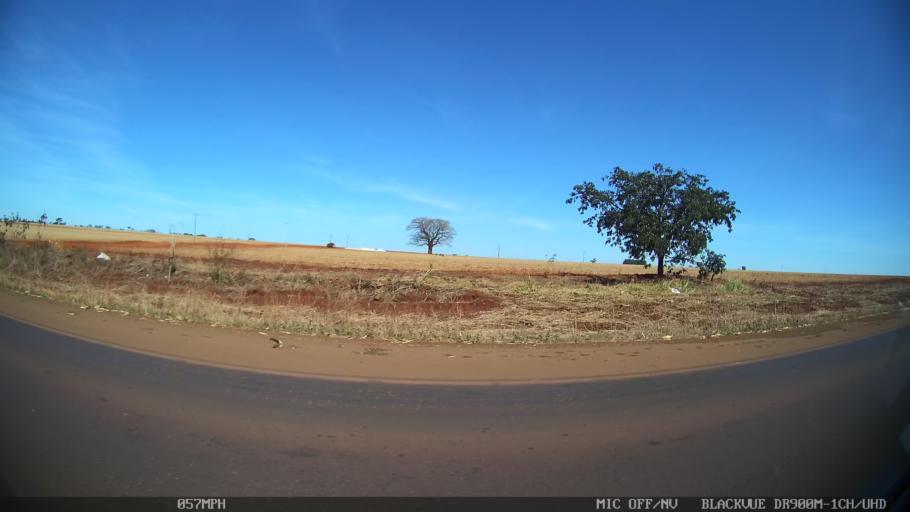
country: BR
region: Sao Paulo
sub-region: Sao Joaquim Da Barra
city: Sao Joaquim da Barra
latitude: -20.5195
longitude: -47.8685
